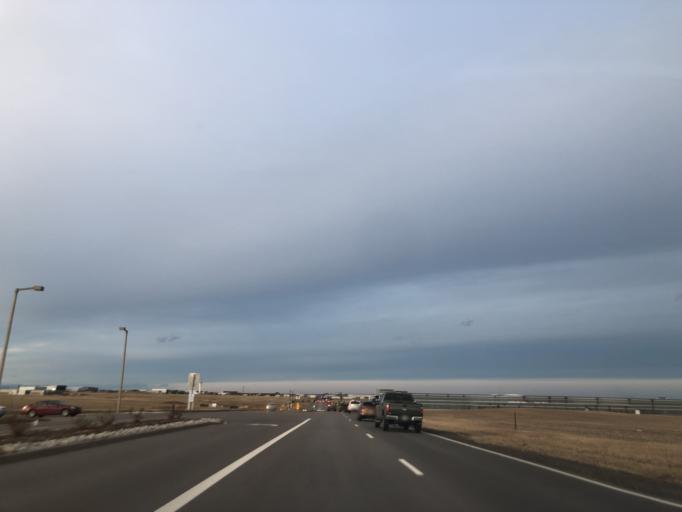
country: US
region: Colorado
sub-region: Douglas County
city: Meridian
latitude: 39.5549
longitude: -104.8393
